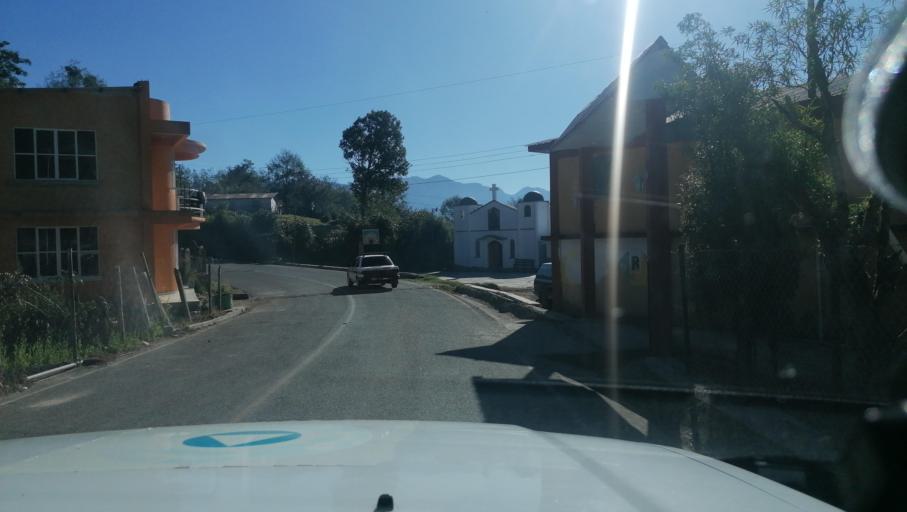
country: MX
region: Chiapas
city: Motozintla de Mendoza
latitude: 15.2477
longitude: -92.2274
